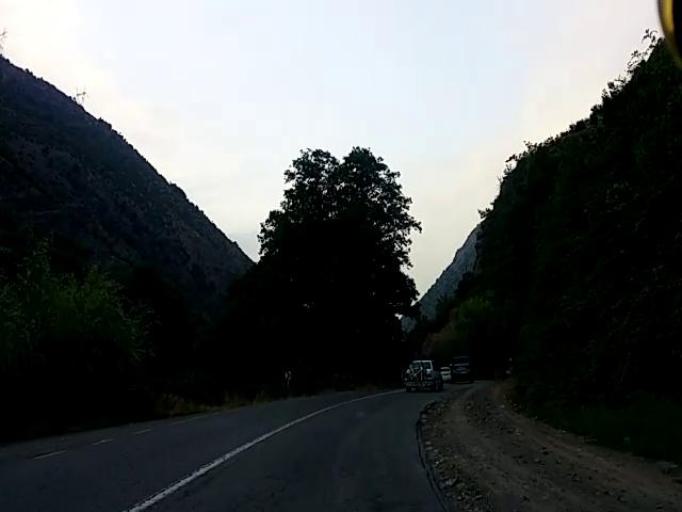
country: IR
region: Mazandaran
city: Chalus
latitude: 36.3276
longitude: 51.2546
